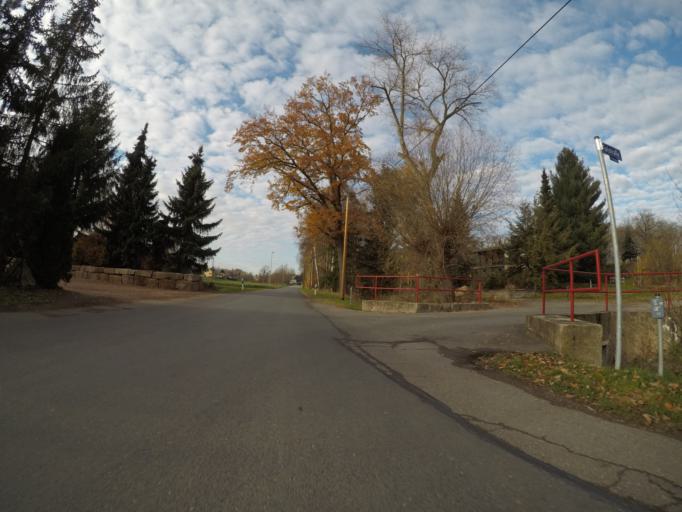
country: DE
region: Thuringia
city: Ponitz
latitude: 50.8561
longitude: 12.3995
